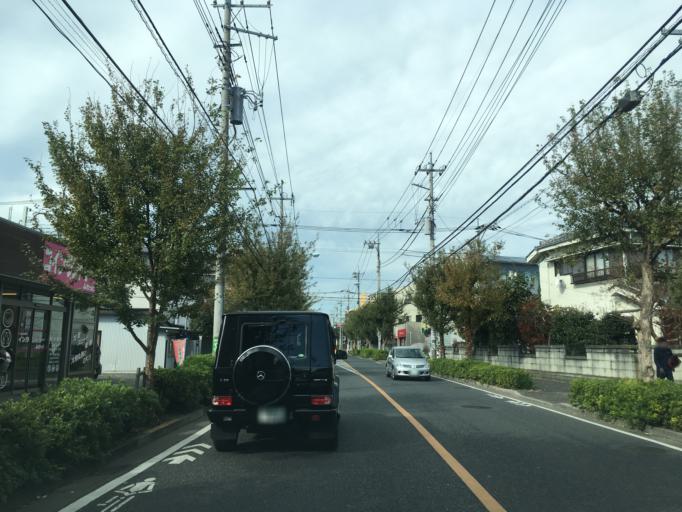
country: JP
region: Tokyo
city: Chofugaoka
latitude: 35.6371
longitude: 139.5755
